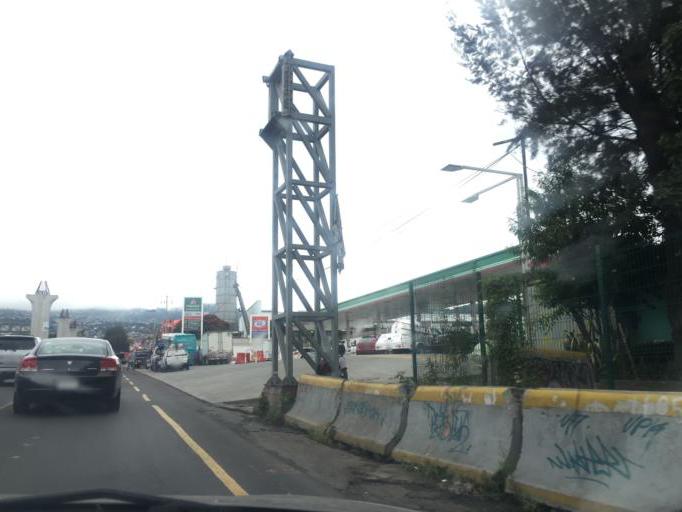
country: MX
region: Mexico City
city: Tlalpan
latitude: 19.2692
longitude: -99.1641
